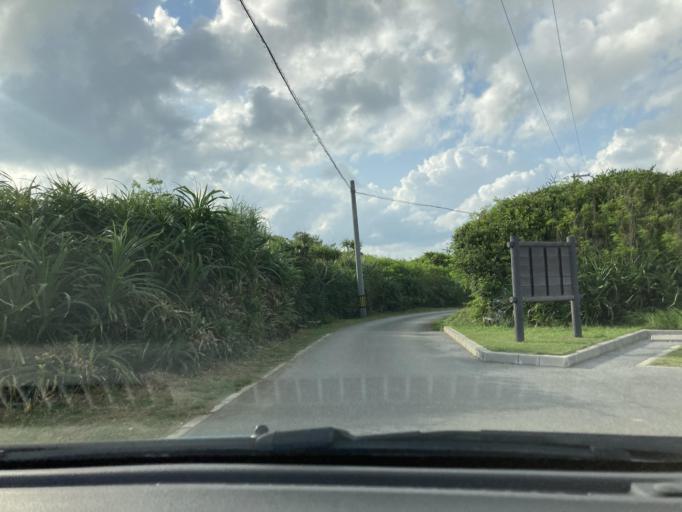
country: JP
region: Okinawa
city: Itoman
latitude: 26.0791
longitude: 127.6691
